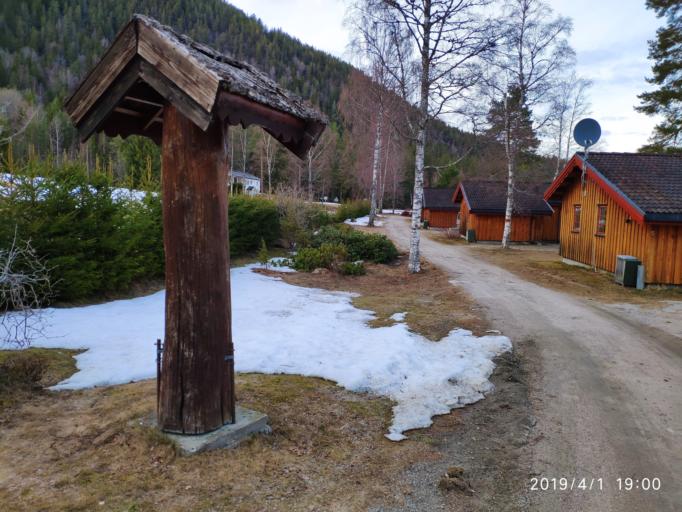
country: NO
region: Telemark
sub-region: Nissedal
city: Treungen
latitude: 59.1193
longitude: 8.4720
